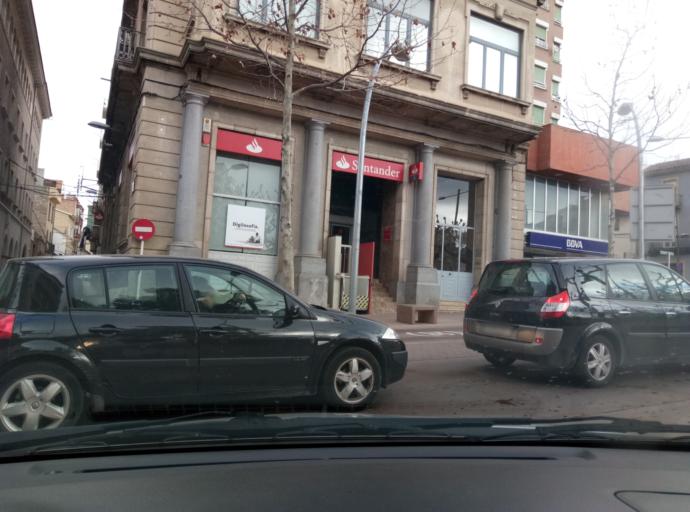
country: ES
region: Catalonia
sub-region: Provincia de Lleida
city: Tarrega
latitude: 41.6484
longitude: 1.1402
